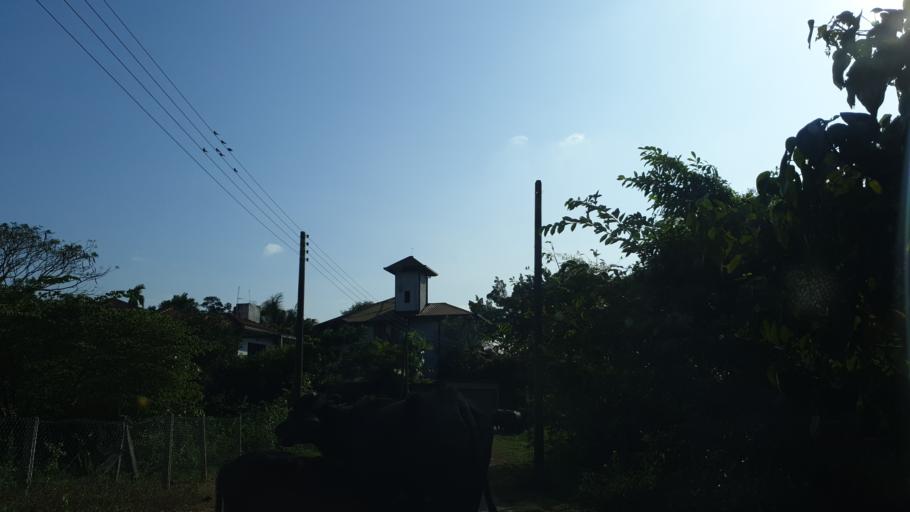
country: LK
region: Western
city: Battaramulla South
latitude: 6.8842
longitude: 79.9484
